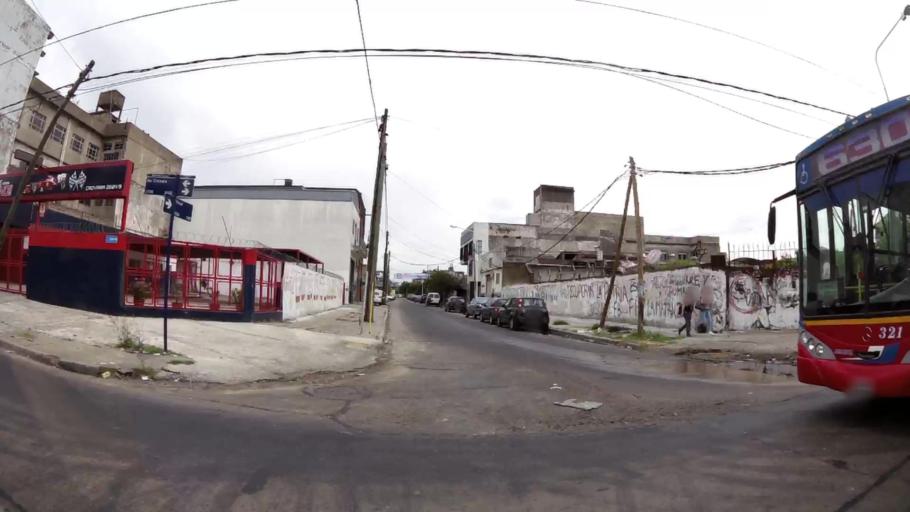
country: AR
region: Buenos Aires
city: San Justo
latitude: -34.6885
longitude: -58.5235
